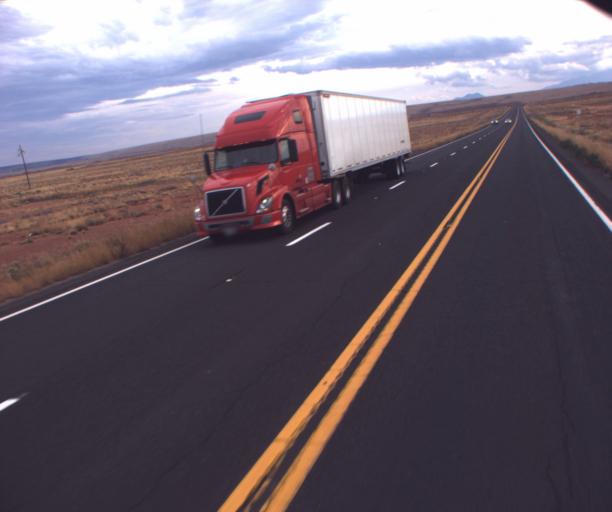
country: US
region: Arizona
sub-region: Coconino County
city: Tuba City
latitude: 35.8074
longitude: -111.4445
